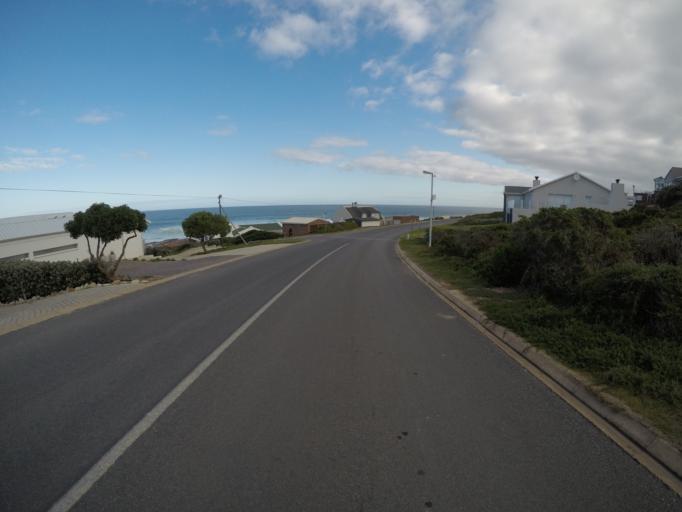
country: ZA
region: Western Cape
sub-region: Eden District Municipality
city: Riversdale
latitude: -34.4321
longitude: 21.3341
